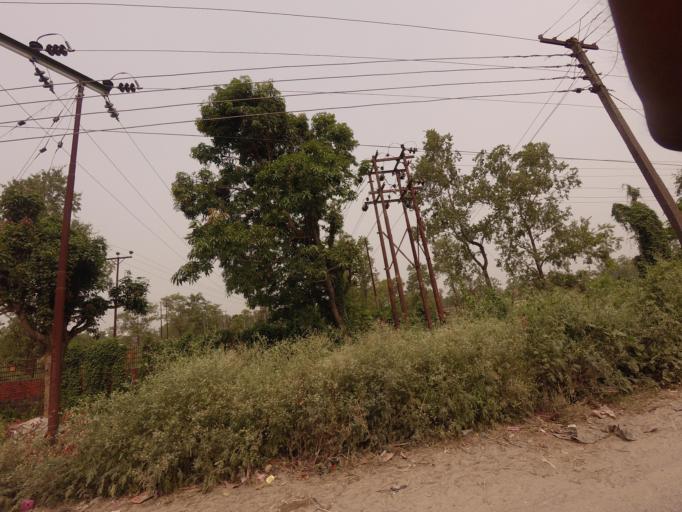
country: IN
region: Uttar Pradesh
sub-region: Maharajganj
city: Nautanwa
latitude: 27.4925
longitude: 83.2843
